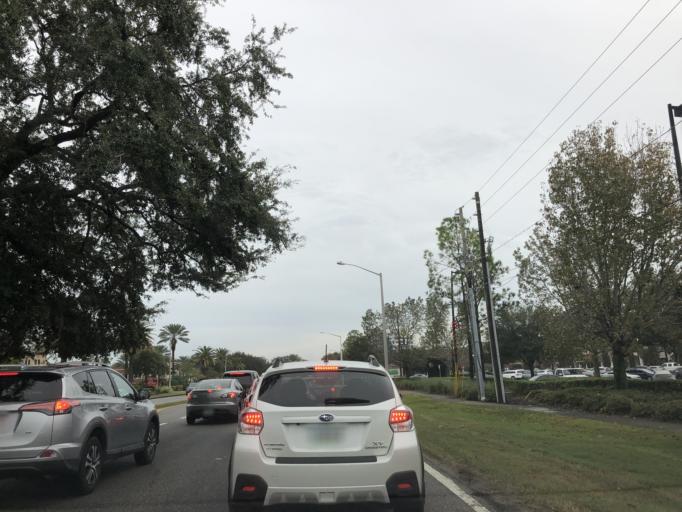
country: US
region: Florida
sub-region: Orange County
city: Doctor Phillips
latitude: 28.4499
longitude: -81.4870
